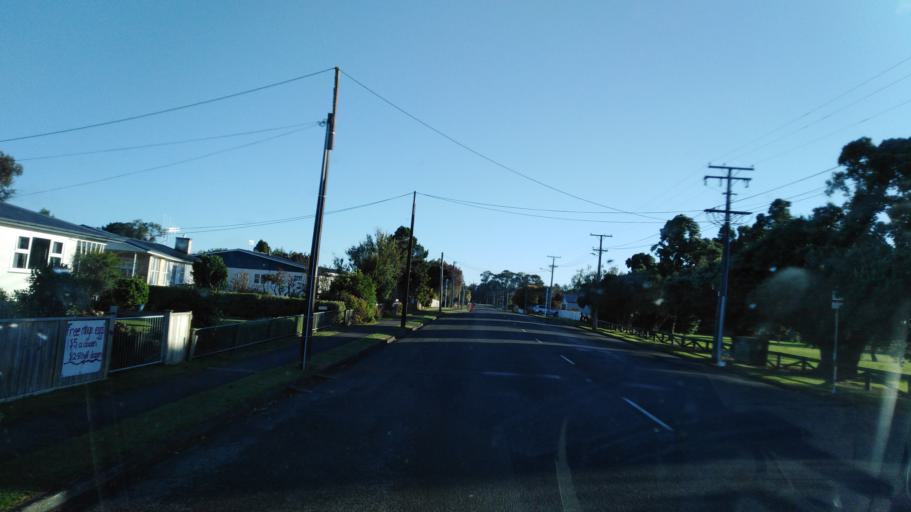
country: NZ
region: Manawatu-Wanganui
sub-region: Rangitikei District
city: Bulls
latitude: -40.0679
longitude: 175.3832
